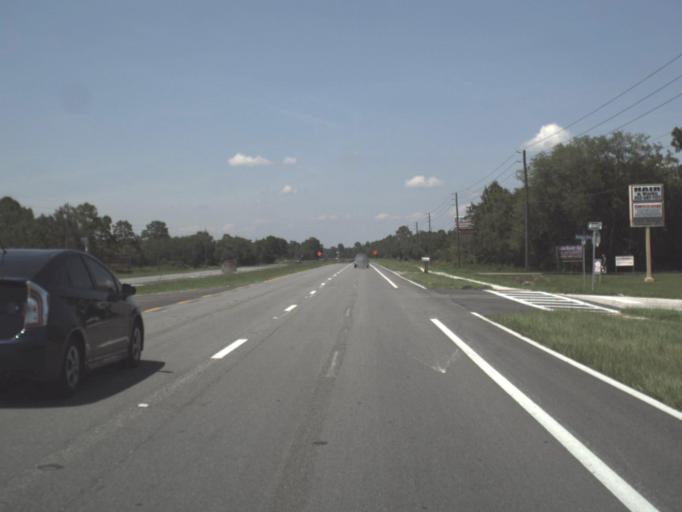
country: US
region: Florida
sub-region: Hernando County
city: North Weeki Wachee
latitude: 28.5879
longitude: -82.5537
